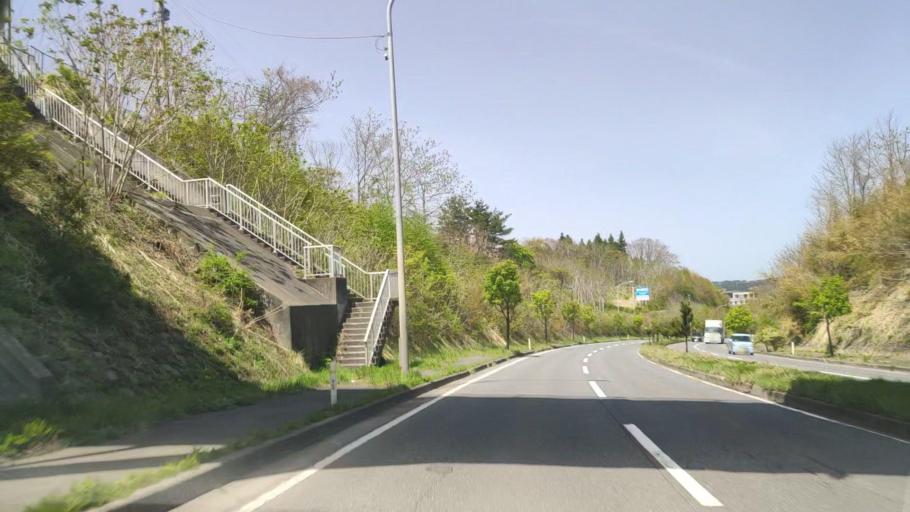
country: JP
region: Aomori
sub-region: Hachinohe Shi
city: Uchimaru
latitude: 40.4966
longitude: 141.4586
